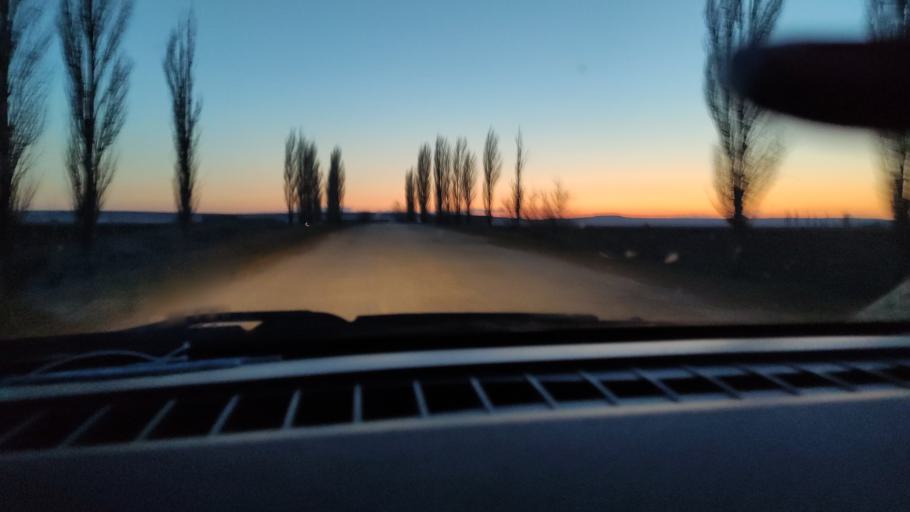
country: RU
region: Saratov
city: Rovnoye
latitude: 50.9382
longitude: 46.1002
